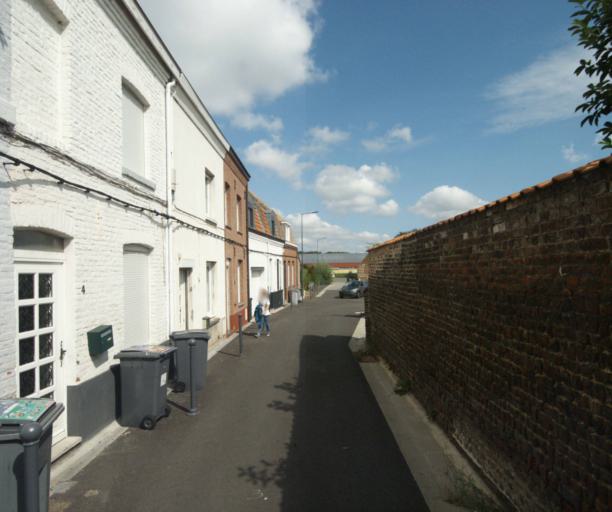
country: FR
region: Nord-Pas-de-Calais
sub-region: Departement du Nord
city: Villeneuve-d'Ascq
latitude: 50.6271
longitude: 3.1513
